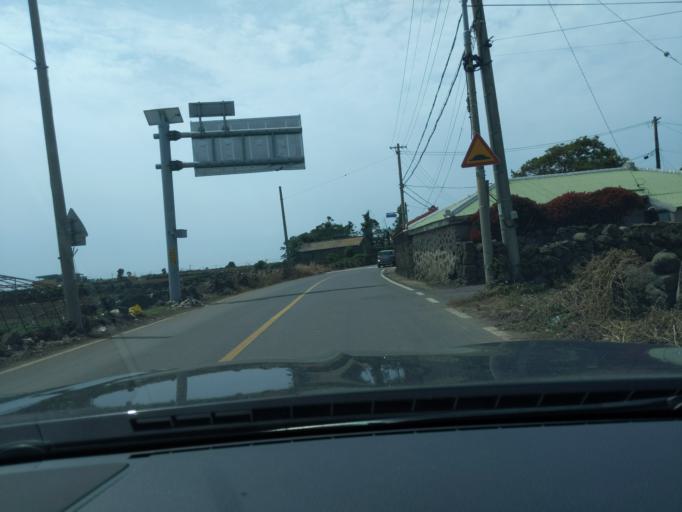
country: KR
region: Jeju-do
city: Gaigeturi
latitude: 33.2246
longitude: 126.2660
